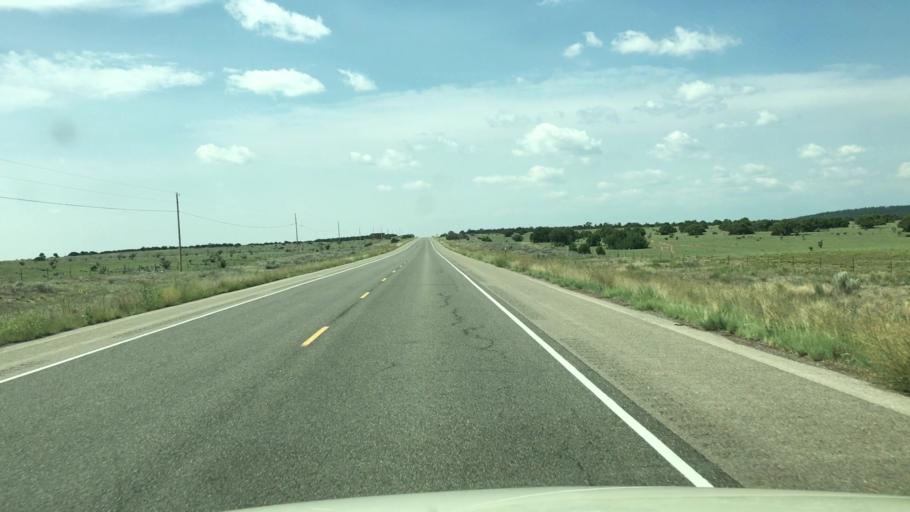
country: US
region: New Mexico
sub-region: Torrance County
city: Moriarty
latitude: 35.0355
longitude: -105.6794
